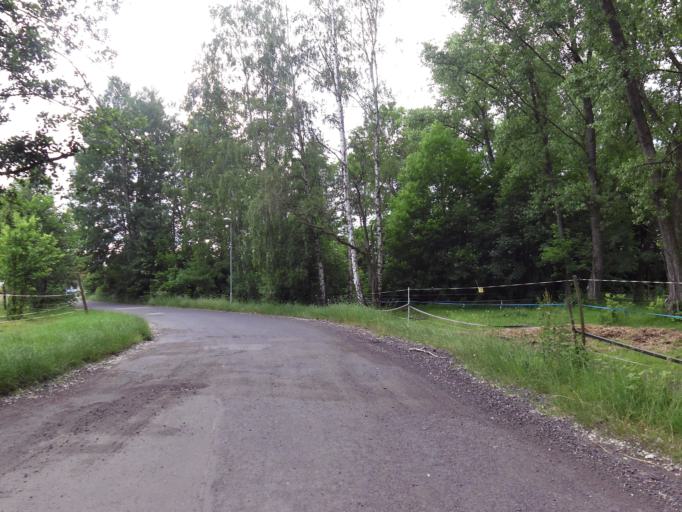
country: CZ
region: Ustecky
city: Varnsdorf
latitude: 50.8895
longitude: 14.6193
